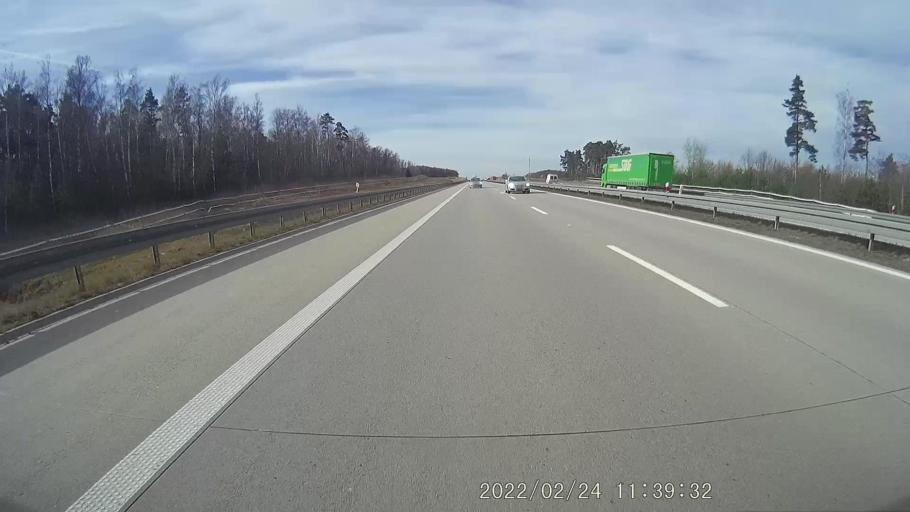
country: PL
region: Lower Silesian Voivodeship
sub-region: Powiat polkowicki
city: Przemkow
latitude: 51.5337
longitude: 15.8652
